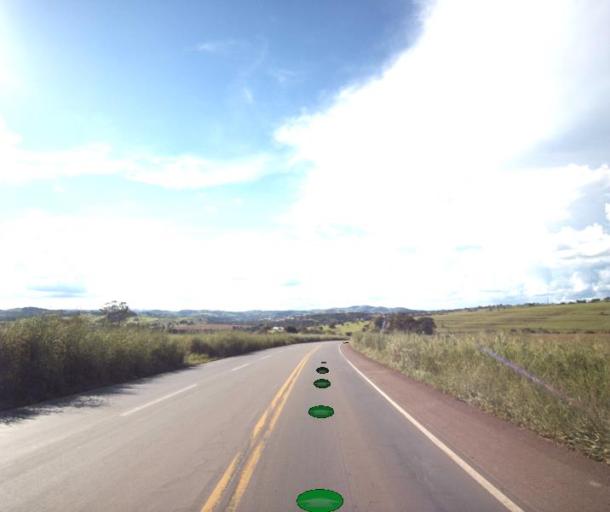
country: BR
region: Goias
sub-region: Rialma
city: Rialma
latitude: -15.3527
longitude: -49.5672
